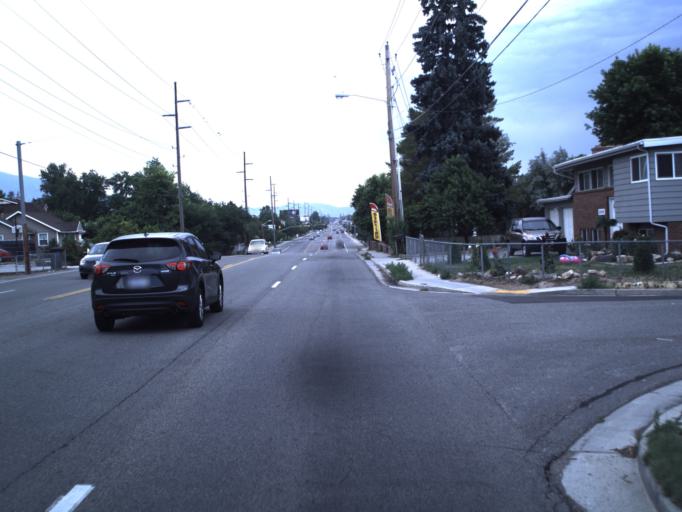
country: US
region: Utah
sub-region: Salt Lake County
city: Murray
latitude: 40.6572
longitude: -111.8660
